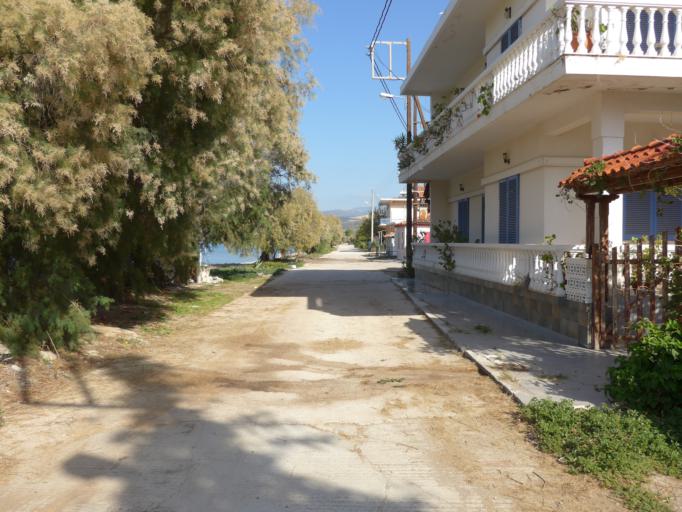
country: GR
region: Peloponnese
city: Asklipieio
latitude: 37.4872
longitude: 22.9923
